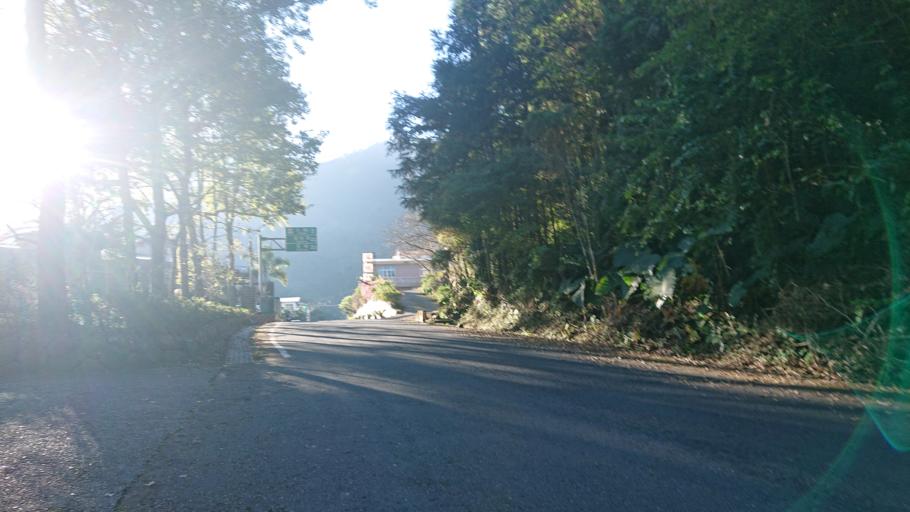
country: TW
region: Taiwan
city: Lugu
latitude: 23.5442
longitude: 120.6875
